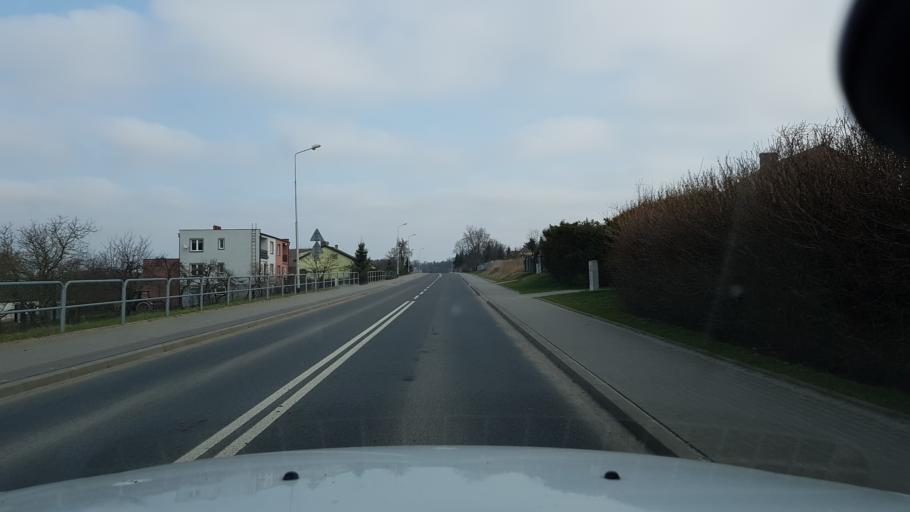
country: PL
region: West Pomeranian Voivodeship
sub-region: Powiat koszalinski
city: Sianow
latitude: 54.2641
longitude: 16.2671
